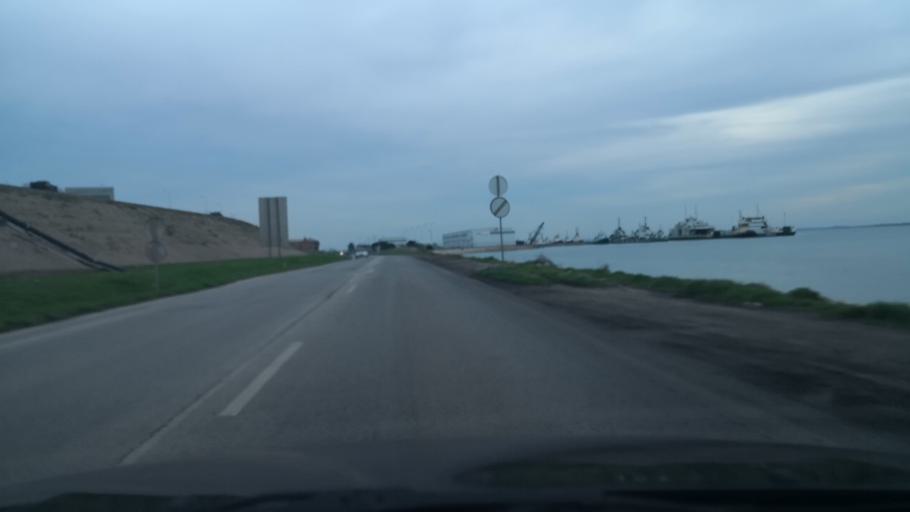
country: PT
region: Setubal
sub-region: Setubal
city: Setubal
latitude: 38.4993
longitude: -8.8392
